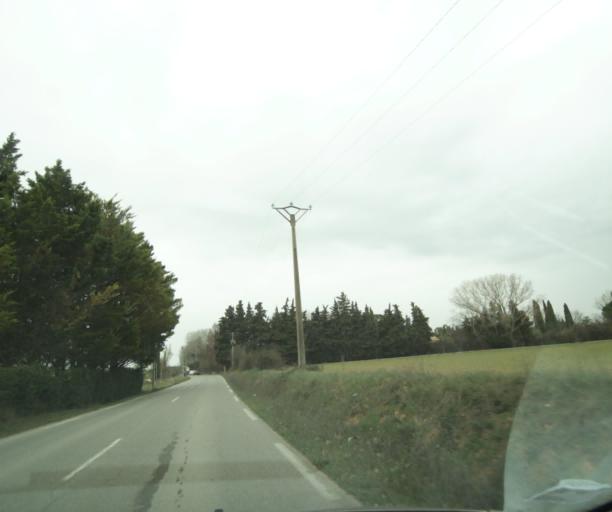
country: FR
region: Provence-Alpes-Cote d'Azur
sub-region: Departement des Bouches-du-Rhone
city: Venelles
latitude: 43.5816
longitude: 5.4642
